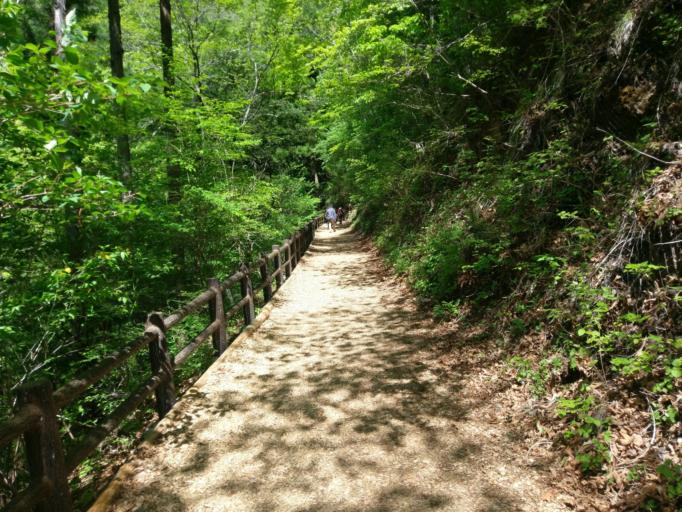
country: JP
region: Yamanashi
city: Uenohara
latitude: 35.7369
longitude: 139.0276
